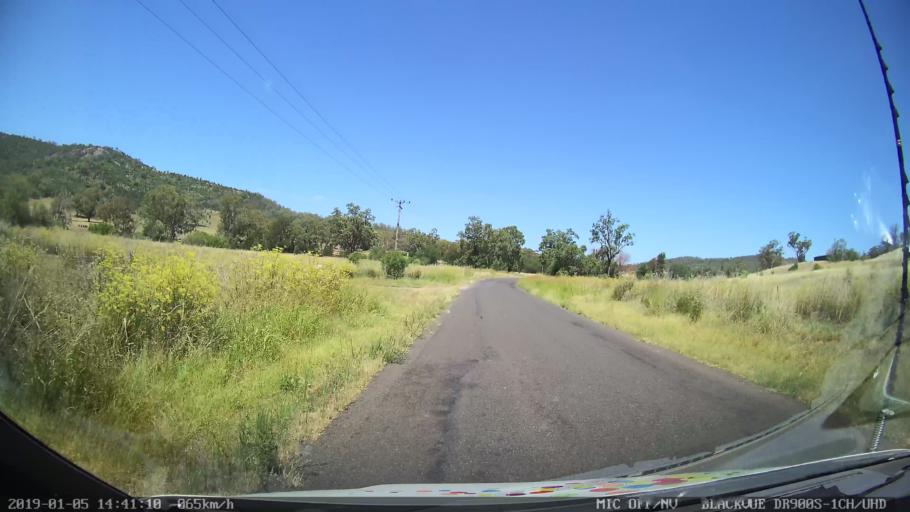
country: AU
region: New South Wales
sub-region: Tamworth Municipality
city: Phillip
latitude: -31.2608
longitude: 150.7216
